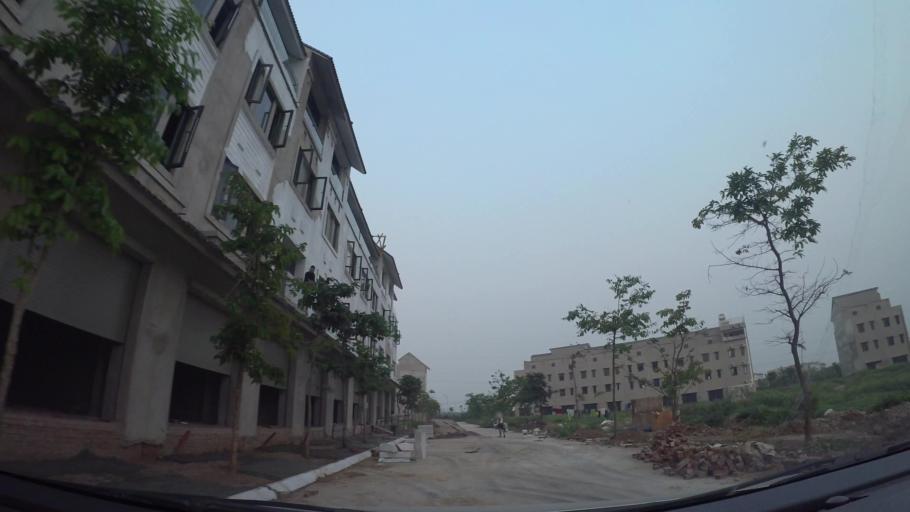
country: VN
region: Ha Noi
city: Ha Dong
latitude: 20.9954
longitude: 105.7335
